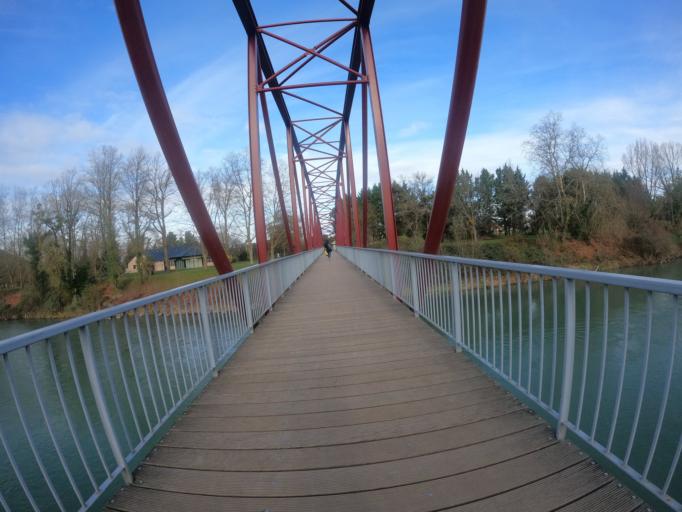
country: FR
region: Aquitaine
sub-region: Departement des Pyrenees-Atlantiques
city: Billere
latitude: 43.2941
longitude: -0.4018
